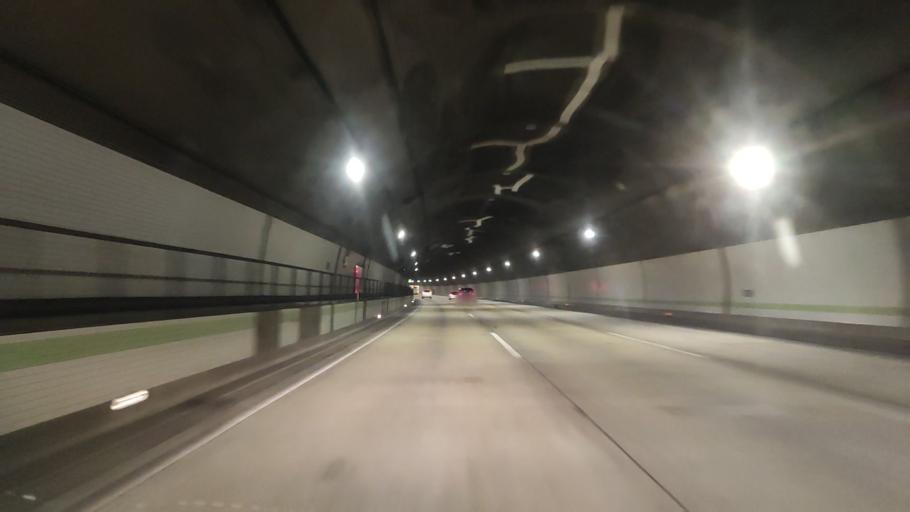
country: JP
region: Hyogo
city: Akashi
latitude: 34.6410
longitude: 135.0450
